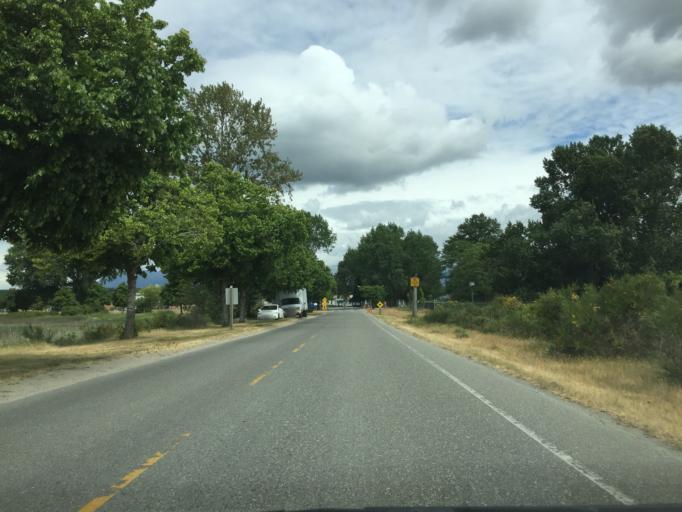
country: CA
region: British Columbia
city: Richmond
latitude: 49.2146
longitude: -123.2017
